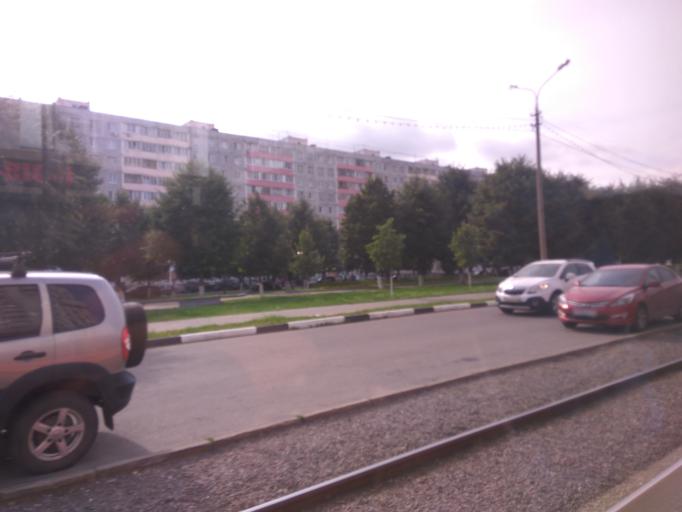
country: RU
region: Moskovskaya
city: Kolomna
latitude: 55.0942
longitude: 38.7651
